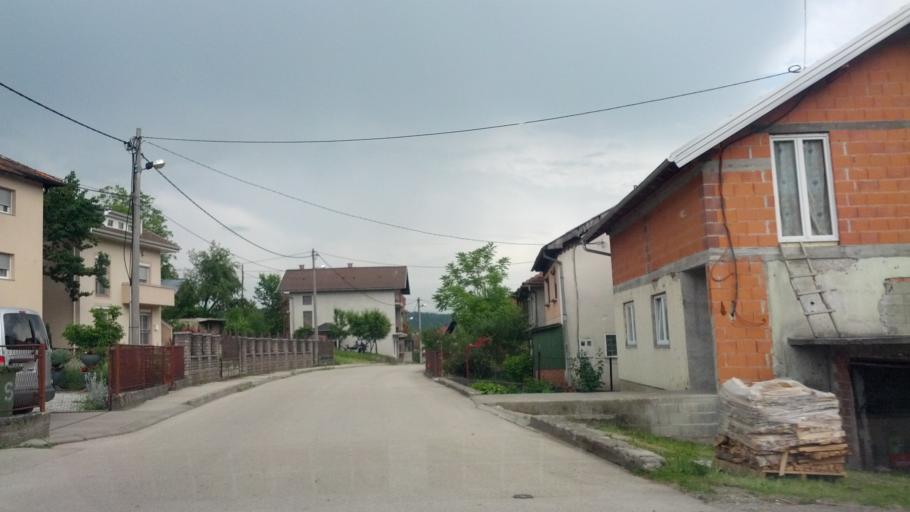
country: BA
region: Federation of Bosnia and Herzegovina
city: Bosanska Krupa
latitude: 44.8872
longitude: 16.1401
